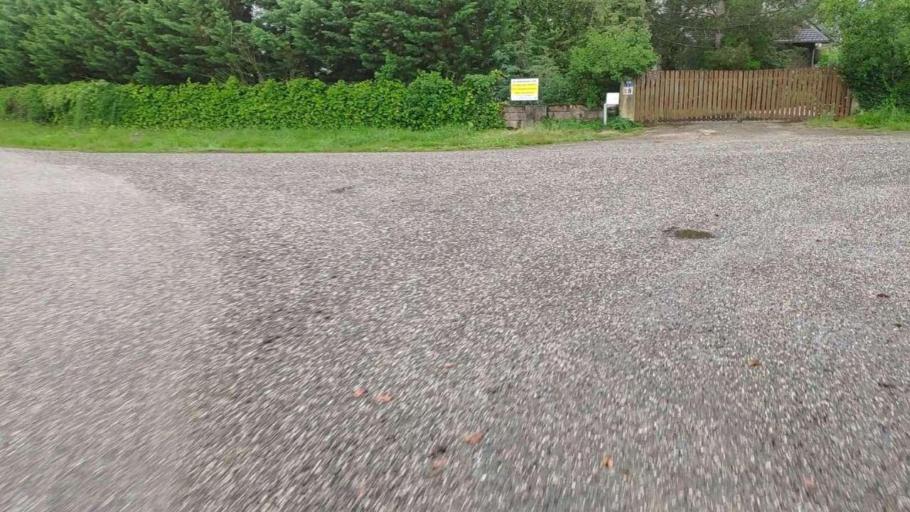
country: FR
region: Franche-Comte
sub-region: Departement du Jura
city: Chaussin
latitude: 46.8772
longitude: 5.4137
